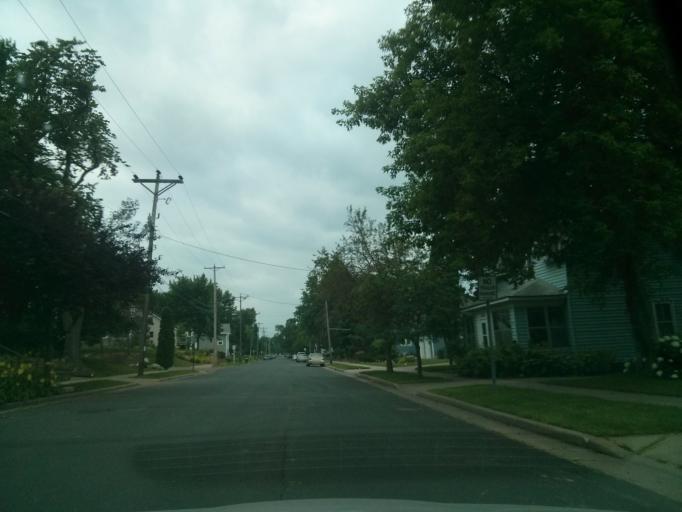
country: US
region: Wisconsin
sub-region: Saint Croix County
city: Hudson
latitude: 44.9808
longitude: -92.7587
